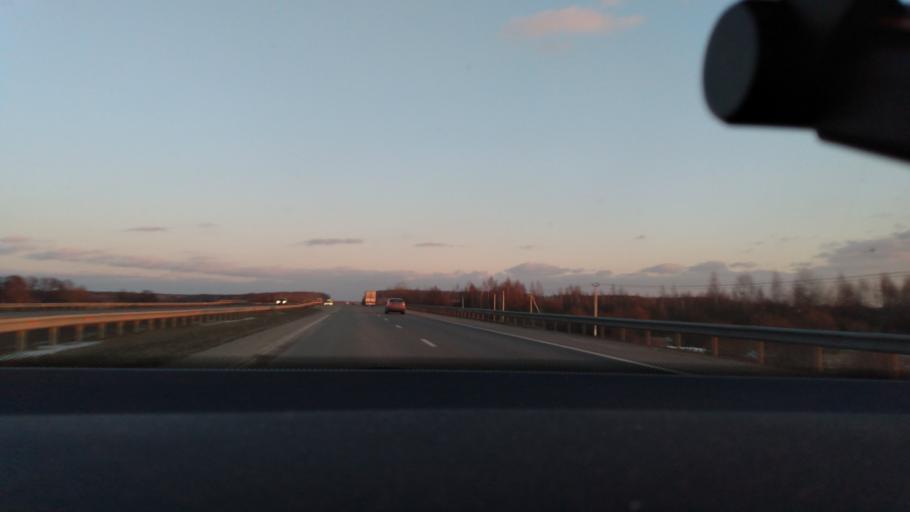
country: RU
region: Moskovskaya
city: Kolomna
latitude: 55.1123
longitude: 38.8616
